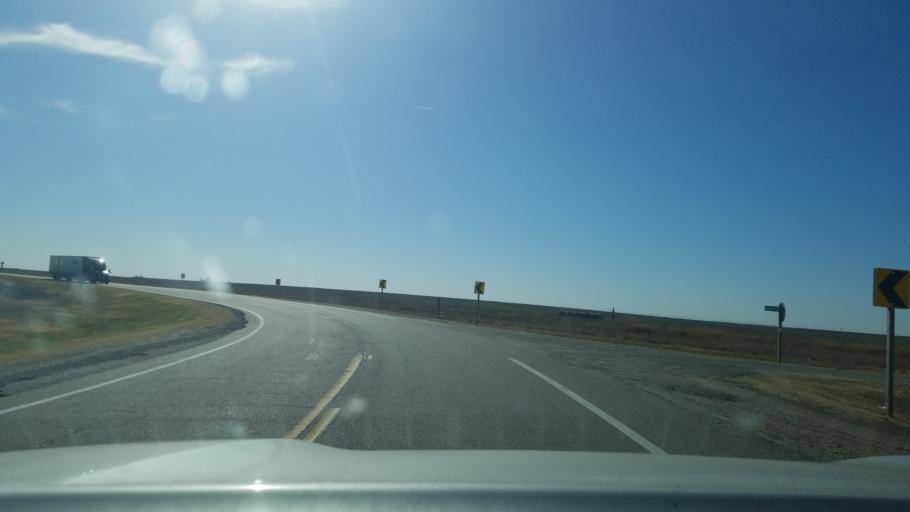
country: US
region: Kansas
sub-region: Ford County
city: Dodge City
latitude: 37.5866
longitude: -99.6828
